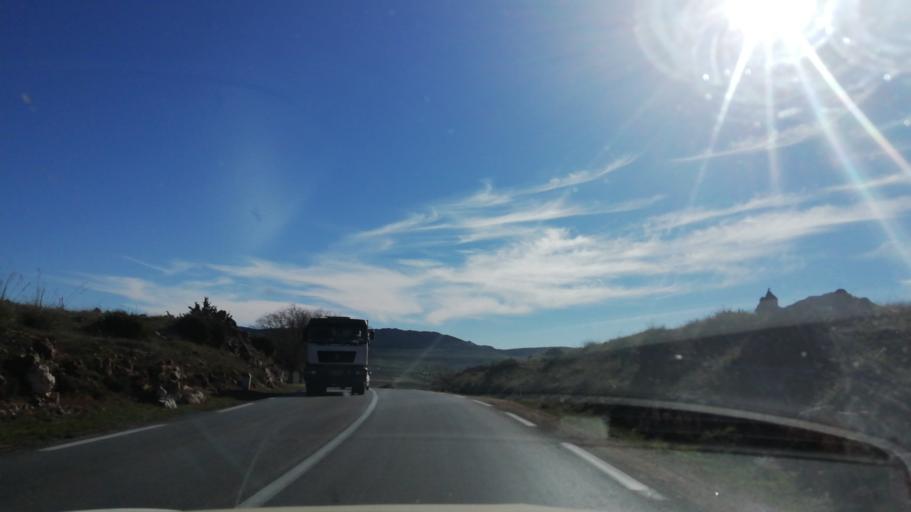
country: DZ
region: Tlemcen
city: Mansoura
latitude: 34.8255
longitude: -1.3691
